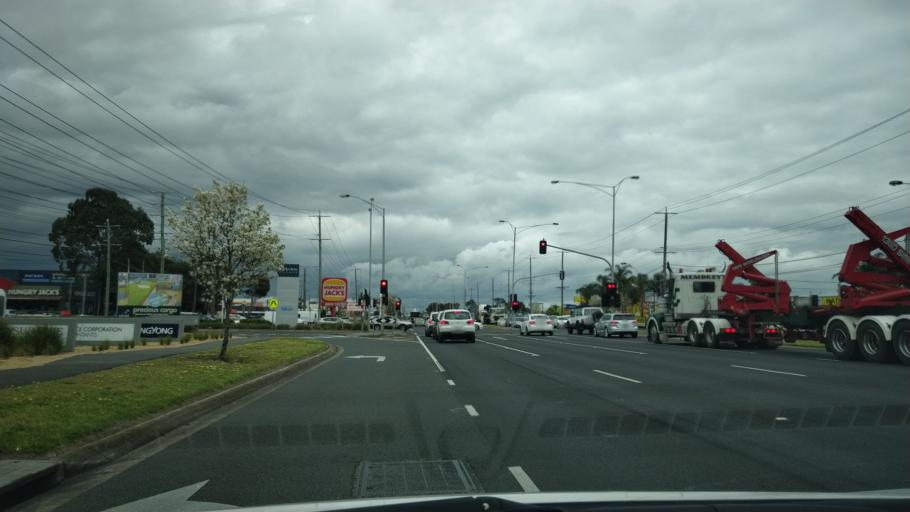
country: AU
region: Victoria
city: Highett
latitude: -37.9493
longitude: 145.0777
